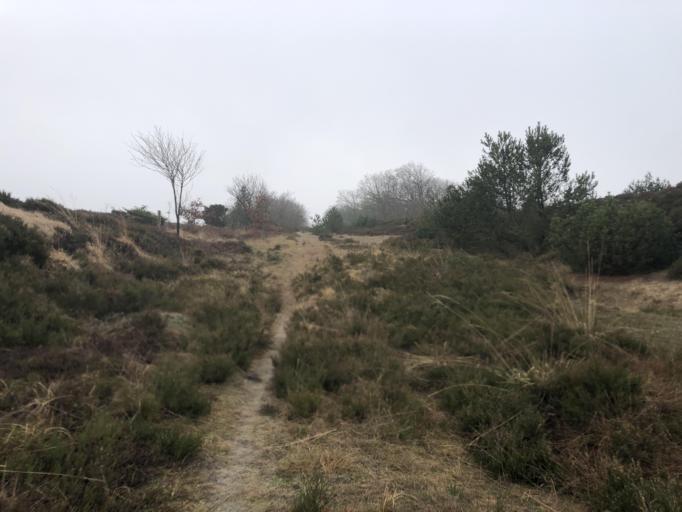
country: DK
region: Central Jutland
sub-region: Holstebro Kommune
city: Holstebro
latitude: 56.2491
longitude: 8.5149
